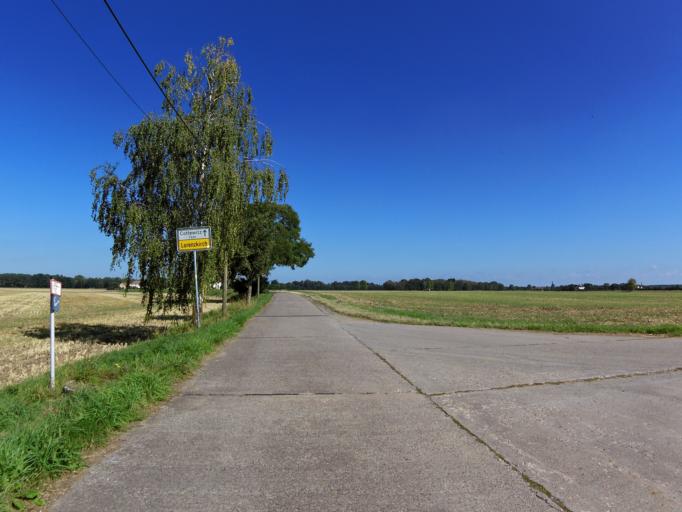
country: DE
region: Saxony
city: Strehla
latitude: 51.3568
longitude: 13.2415
